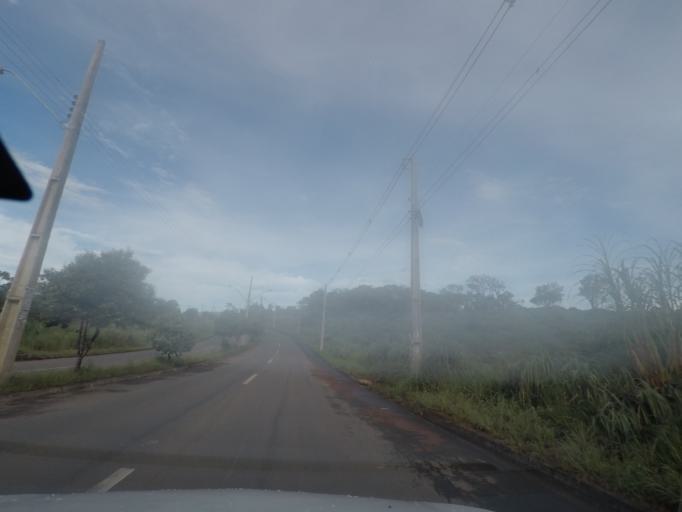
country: BR
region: Goias
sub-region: Aparecida De Goiania
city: Aparecida de Goiania
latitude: -16.7845
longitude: -49.3769
